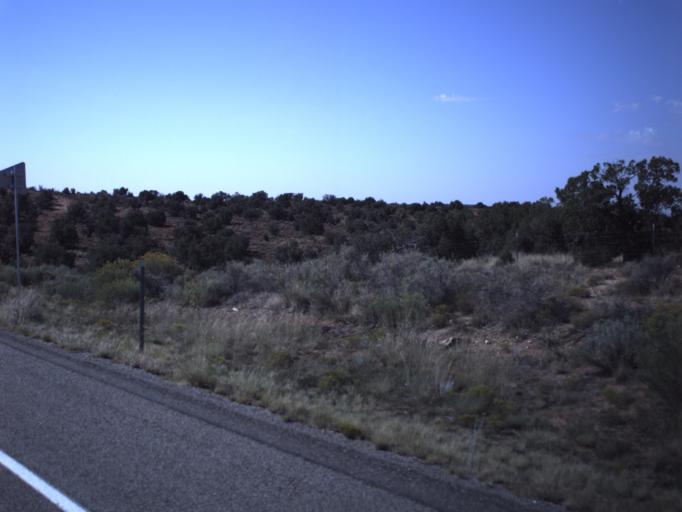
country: US
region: Utah
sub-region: San Juan County
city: Blanding
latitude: 37.4765
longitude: -109.4675
